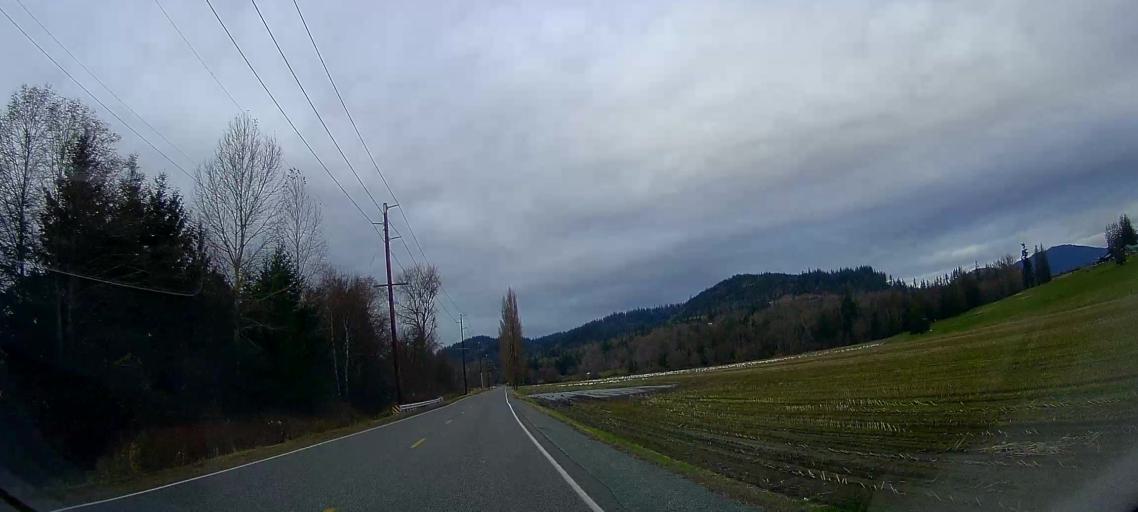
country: US
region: Washington
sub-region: Skagit County
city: Sedro-Woolley
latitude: 48.5239
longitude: -122.2721
